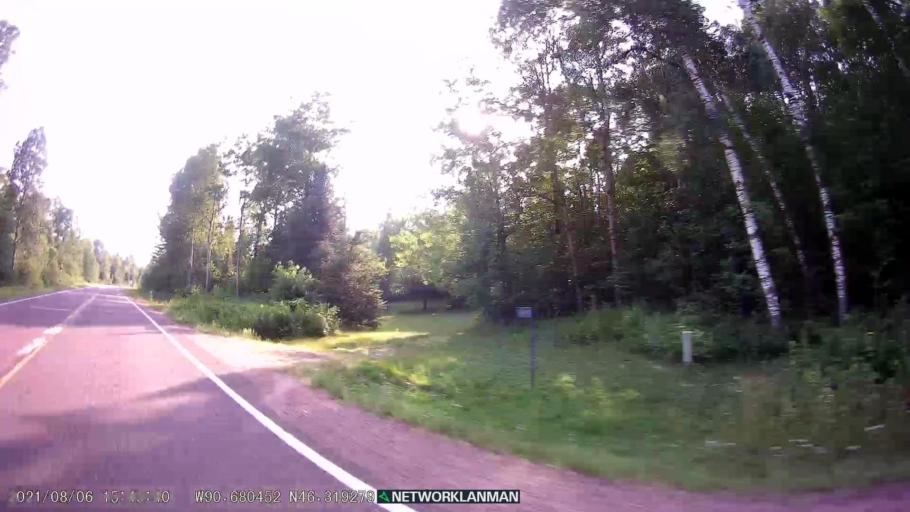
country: US
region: Wisconsin
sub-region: Ashland County
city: Ashland
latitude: 46.3190
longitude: -90.6807
